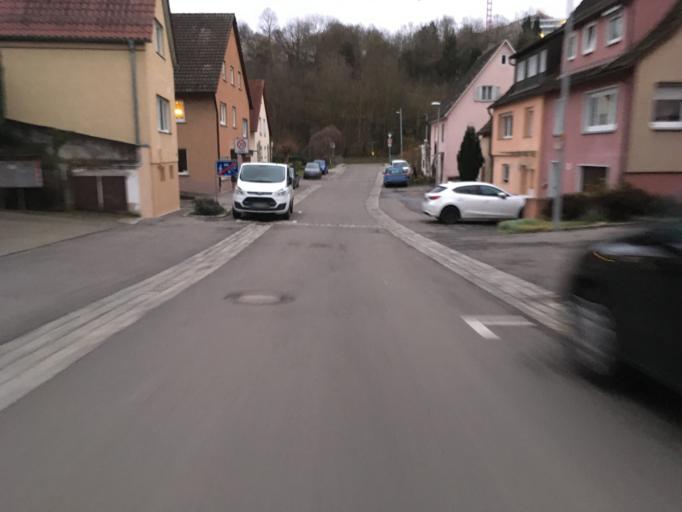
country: DE
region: Baden-Wuerttemberg
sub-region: Regierungsbezirk Stuttgart
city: Kornwestheim
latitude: 48.8400
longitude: 9.1994
